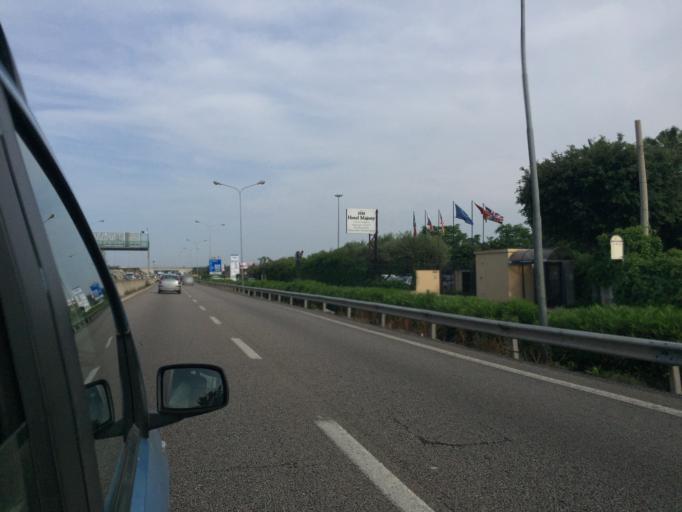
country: IT
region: Apulia
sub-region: Provincia di Bari
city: Triggiano
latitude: 41.0984
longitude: 16.9361
